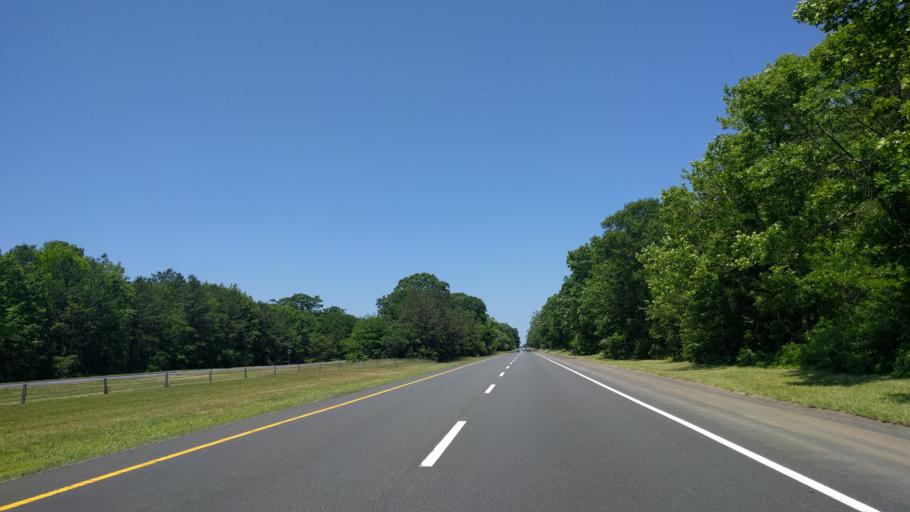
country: US
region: New York
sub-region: Suffolk County
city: Eastport
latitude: 40.8542
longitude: -72.7533
